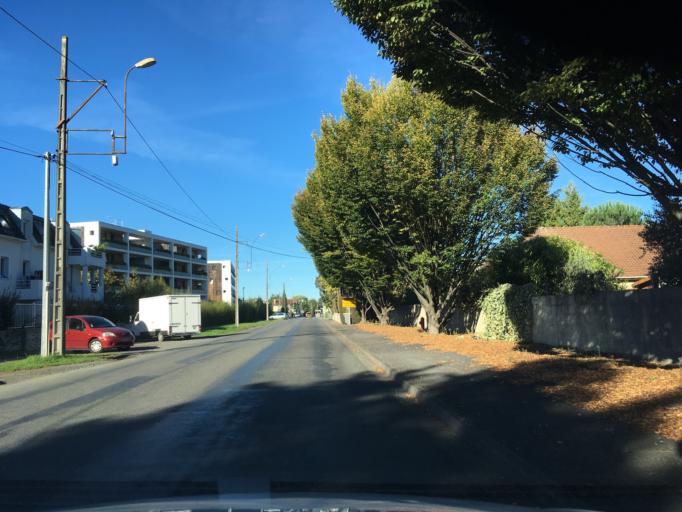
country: FR
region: Aquitaine
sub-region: Departement des Pyrenees-Atlantiques
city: Idron
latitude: 43.3134
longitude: -0.3304
